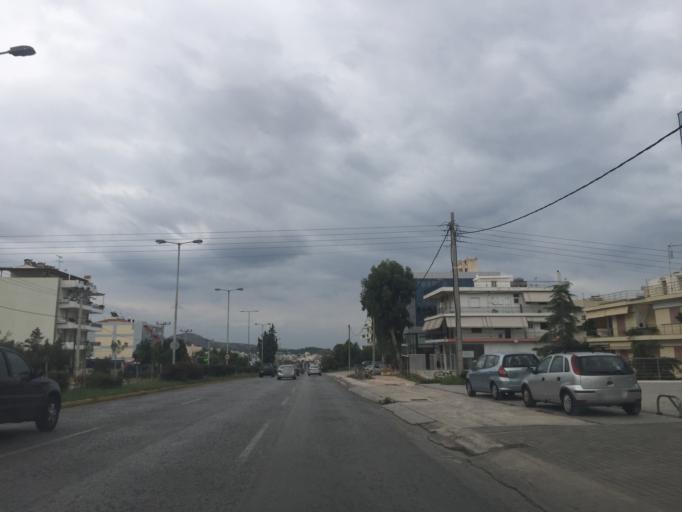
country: GR
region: Attica
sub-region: Nomarchia Anatolikis Attikis
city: Voula
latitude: 37.8480
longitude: 23.7690
